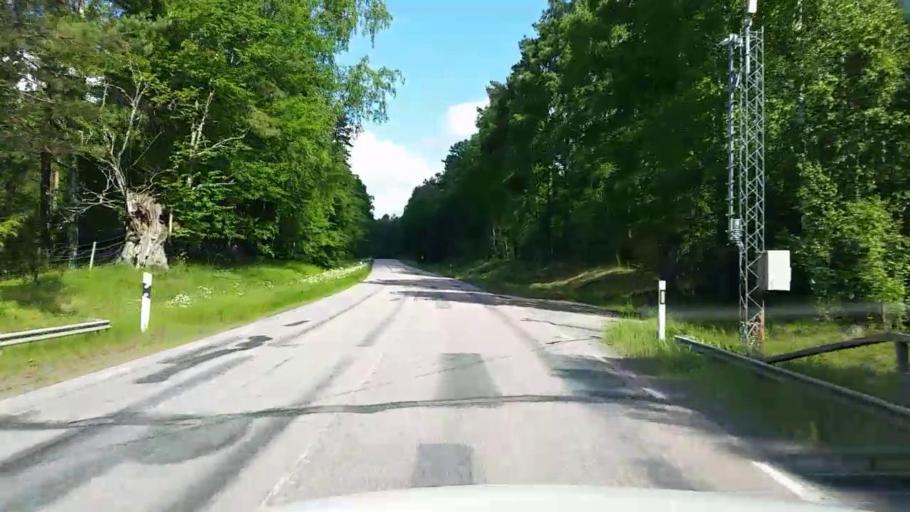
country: SE
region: Vaestmanland
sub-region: Kopings Kommun
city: Kolsva
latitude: 59.6708
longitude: 15.7712
